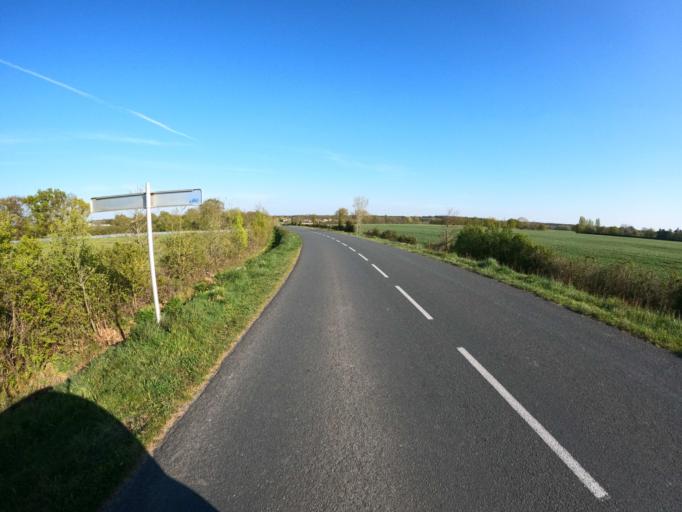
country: FR
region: Pays de la Loire
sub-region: Departement de la Vendee
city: Les Brouzils
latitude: 46.8804
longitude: -1.3313
